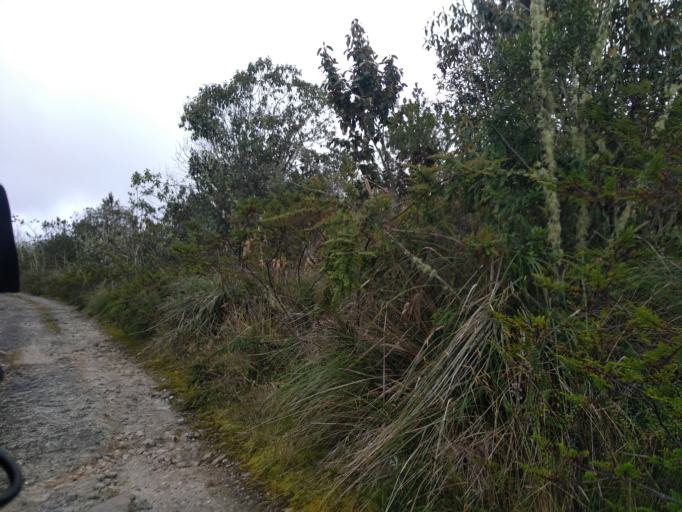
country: EC
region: Carchi
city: San Gabriel
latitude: 0.7023
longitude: -77.8409
